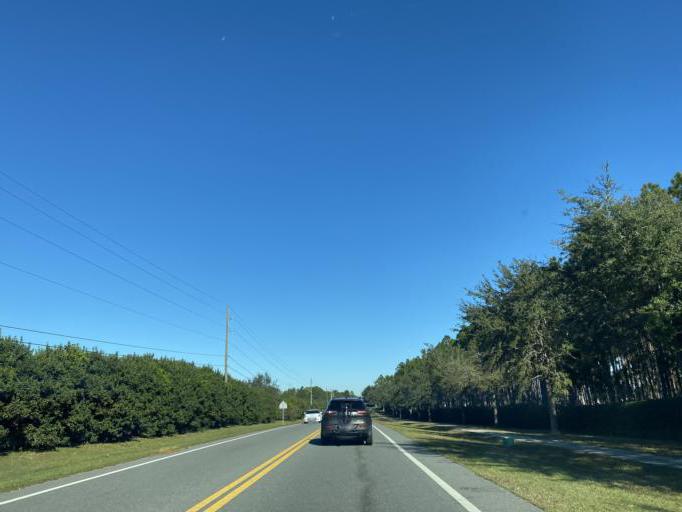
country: US
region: Florida
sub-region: Lake County
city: Minneola
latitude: 28.5158
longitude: -81.7070
